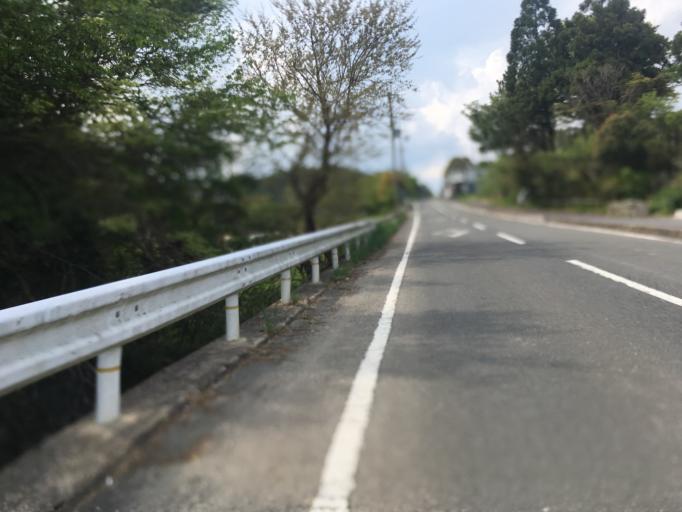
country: JP
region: Kyoto
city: Kameoka
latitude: 35.1095
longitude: 135.5770
